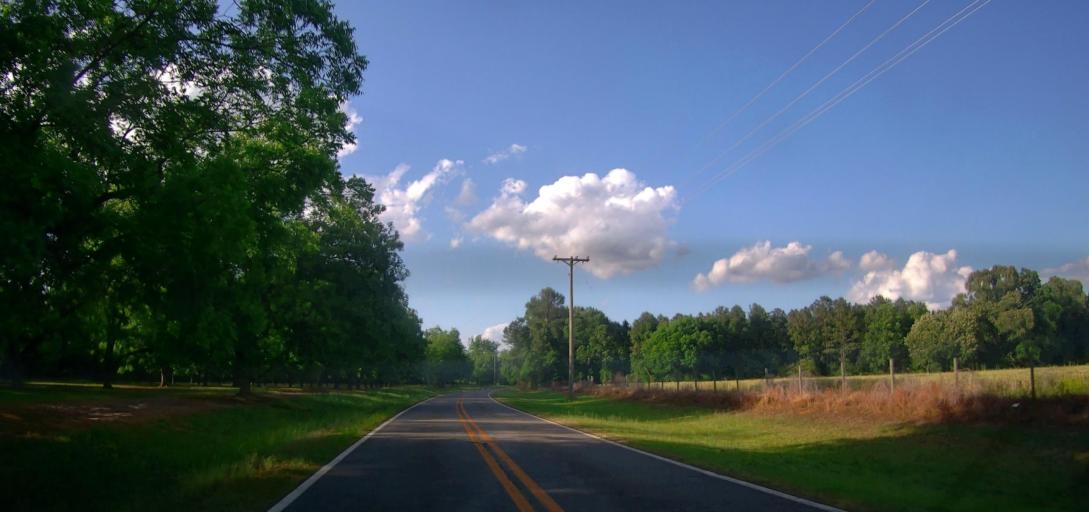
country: US
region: Georgia
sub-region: Peach County
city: Byron
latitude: 32.6677
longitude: -83.8022
